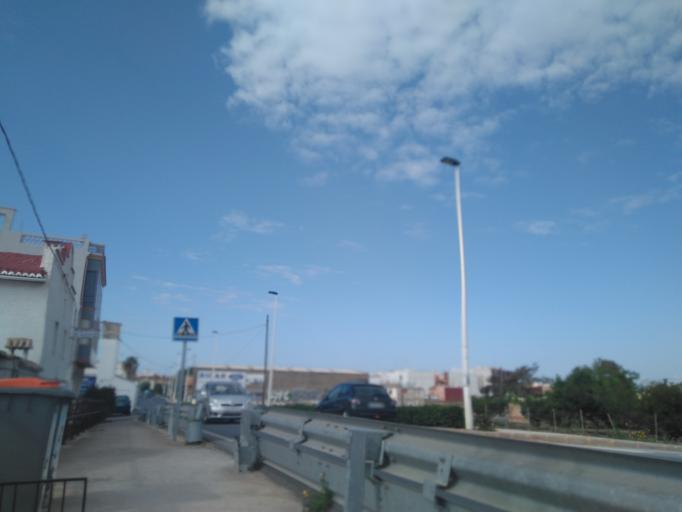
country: ES
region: Valencia
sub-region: Provincia de Valencia
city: Alboraya
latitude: 39.5047
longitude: -0.3447
